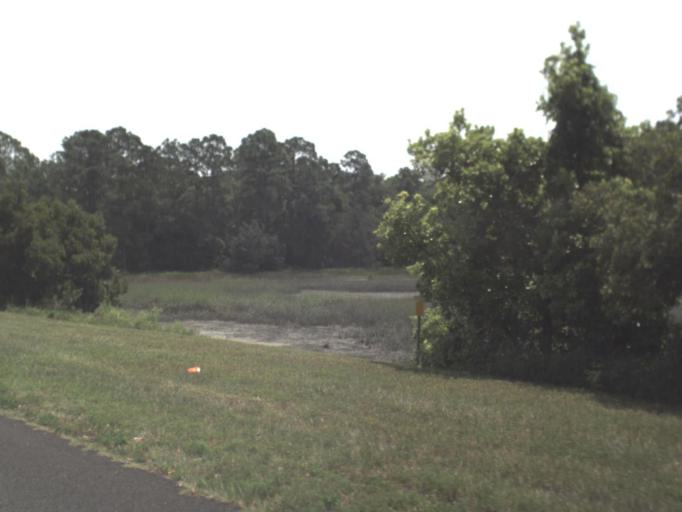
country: US
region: Florida
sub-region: Nassau County
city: Fernandina Beach
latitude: 30.6185
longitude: -81.5024
